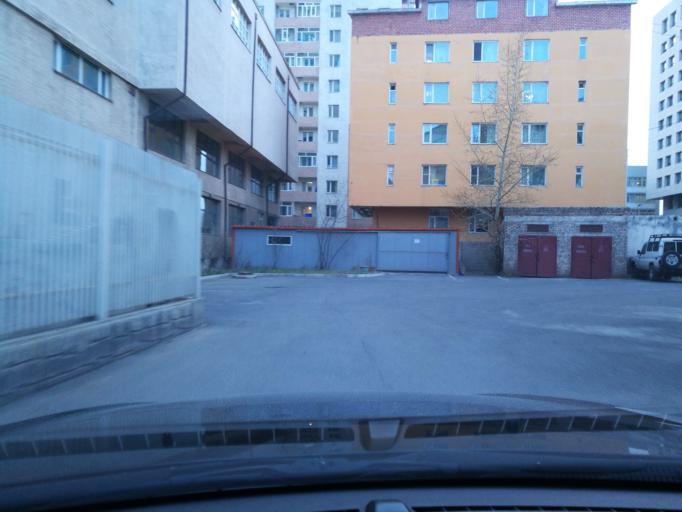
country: MN
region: Ulaanbaatar
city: Ulaanbaatar
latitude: 47.9242
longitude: 106.9209
